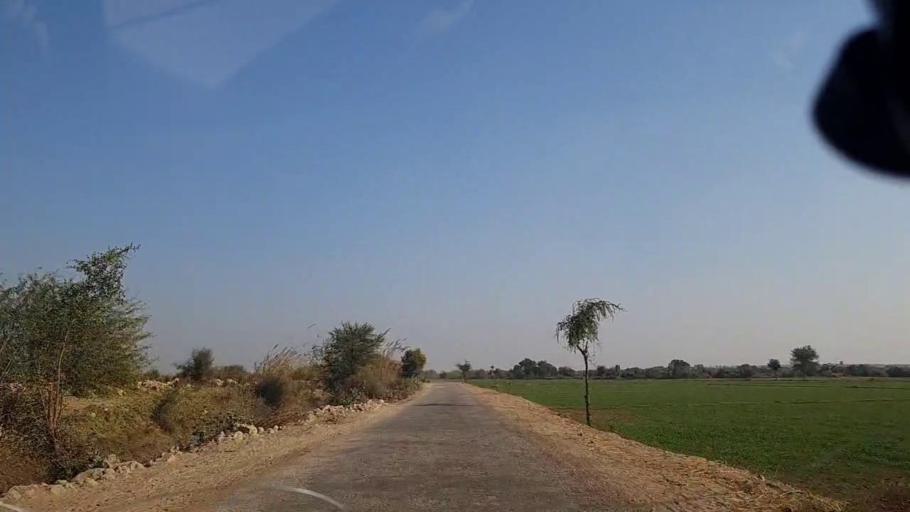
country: PK
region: Sindh
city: Khanpur
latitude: 27.6833
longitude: 69.5311
